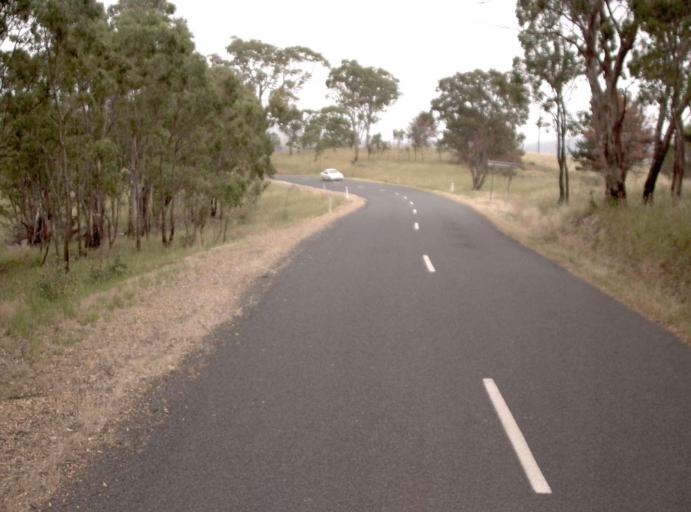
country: AU
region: Victoria
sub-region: Wellington
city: Heyfield
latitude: -37.8721
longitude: 146.7085
